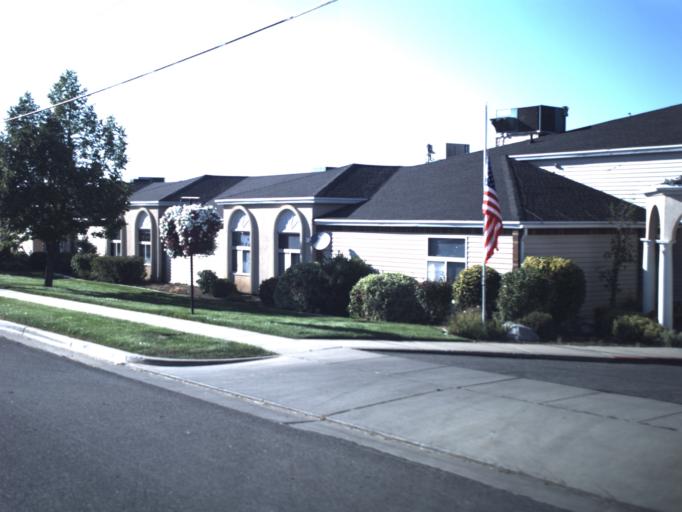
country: US
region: Utah
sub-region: Davis County
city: Clinton
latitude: 41.1399
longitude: -112.0591
